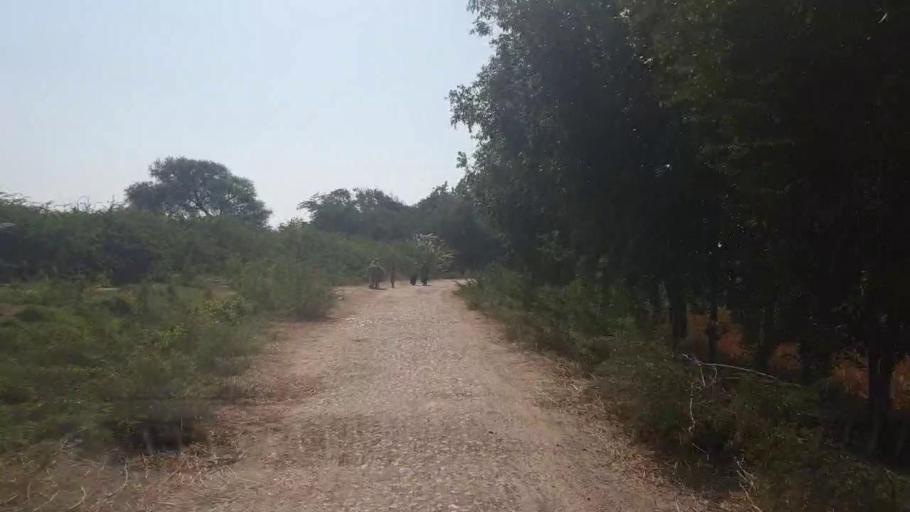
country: PK
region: Sindh
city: Badin
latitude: 24.6736
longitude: 68.8820
